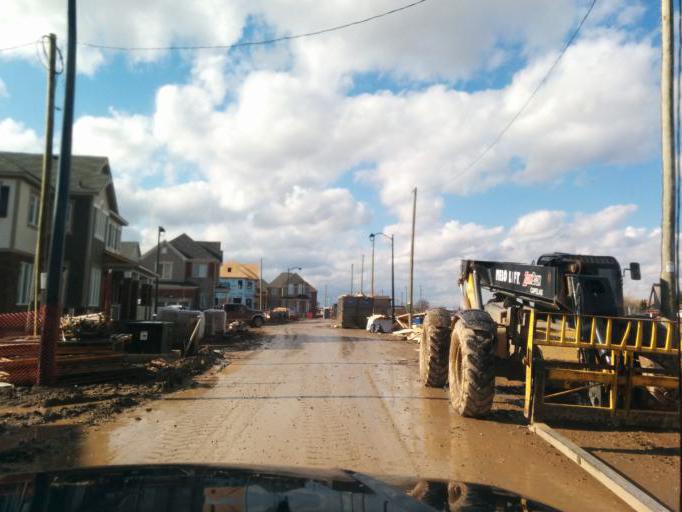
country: CA
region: Ontario
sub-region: Halton
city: Milton
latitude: 43.4863
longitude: -79.8379
